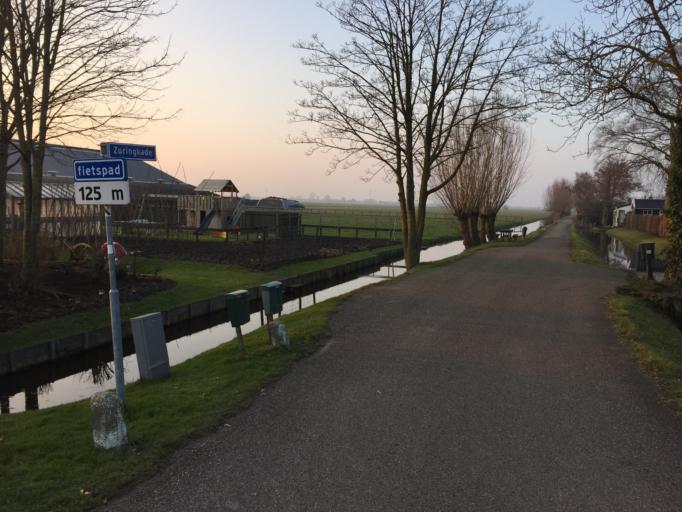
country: NL
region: Utrecht
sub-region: Gemeente Oudewater
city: Oudewater
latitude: 52.0220
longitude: 4.8574
